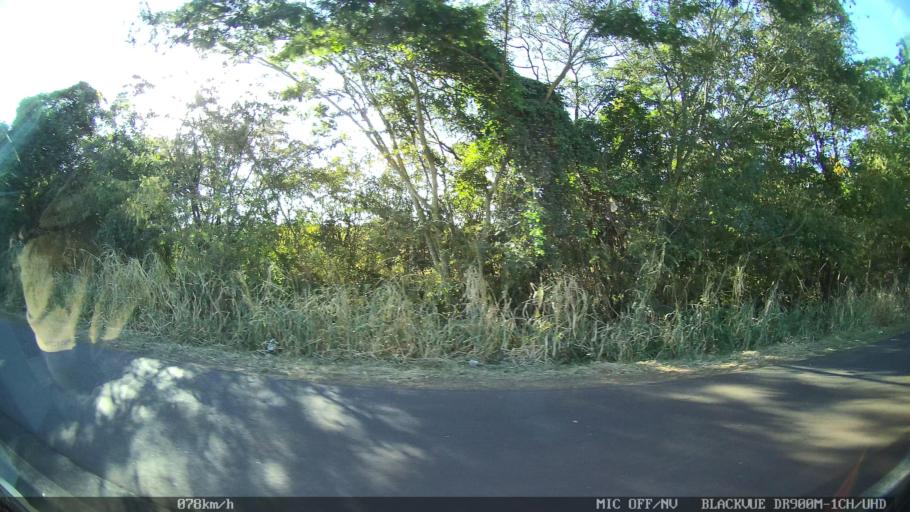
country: BR
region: Sao Paulo
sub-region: Guapiacu
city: Guapiacu
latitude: -20.7540
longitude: -49.1492
